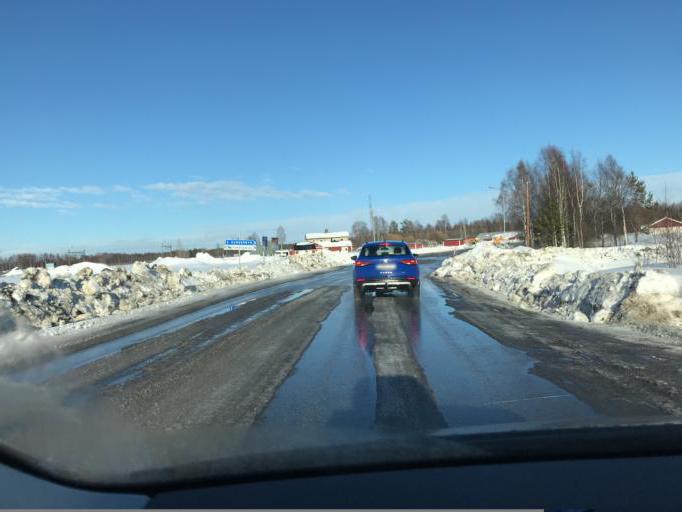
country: SE
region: Norrbotten
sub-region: Lulea Kommun
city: Sodra Sunderbyn
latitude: 65.6640
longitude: 21.9532
